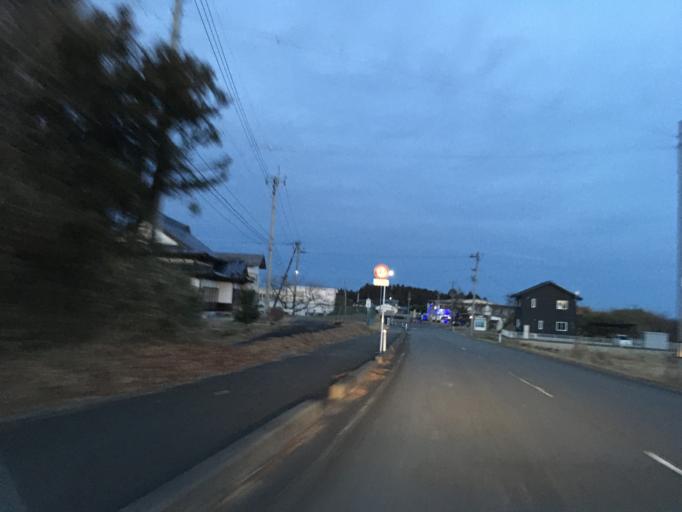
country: JP
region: Miyagi
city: Wakuya
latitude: 38.6981
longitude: 141.1073
